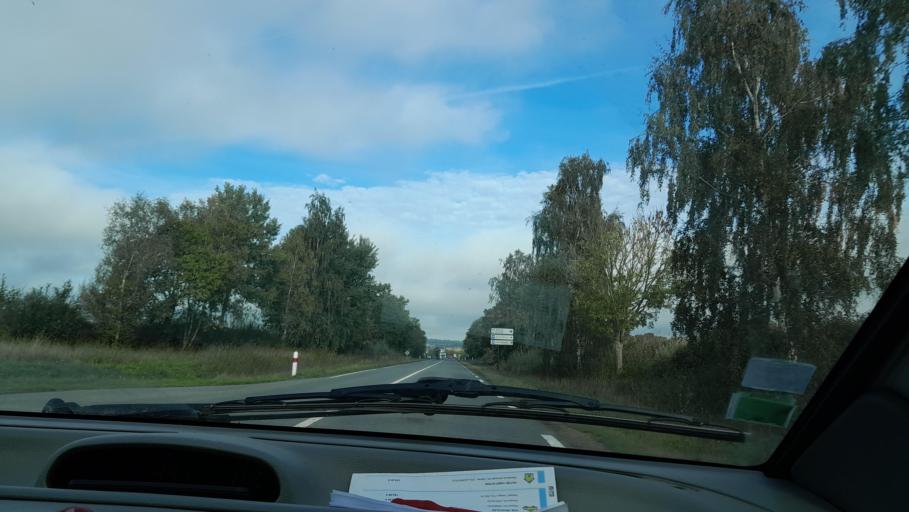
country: FR
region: Brittany
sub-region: Departement d'Ille-et-Vilaine
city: Beauce
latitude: 48.3140
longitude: -1.1812
